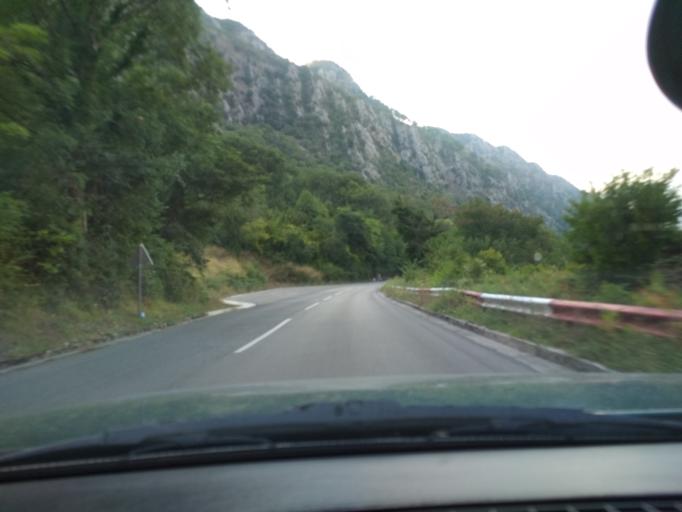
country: ME
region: Kotor
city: Kotor
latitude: 42.4129
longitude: 18.7625
